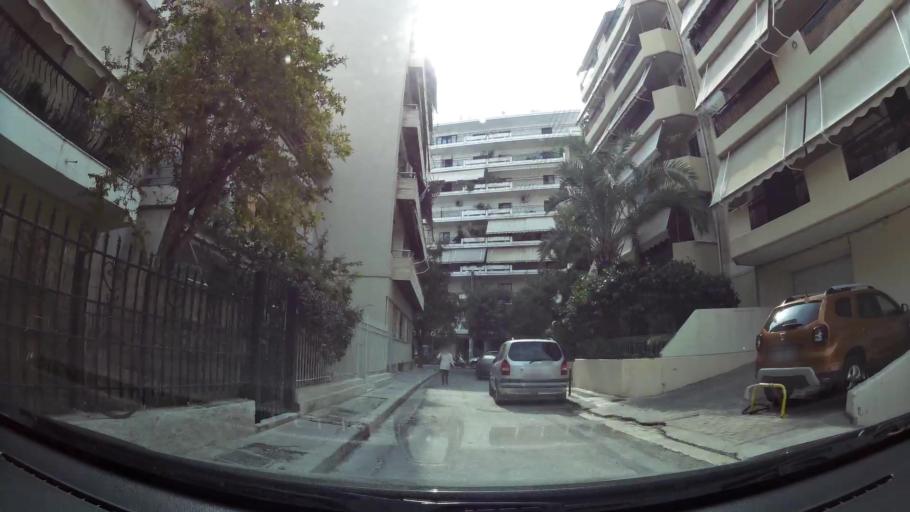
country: GR
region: Attica
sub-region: Nomarchia Athinas
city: Moskhaton
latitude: 37.9501
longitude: 23.6668
